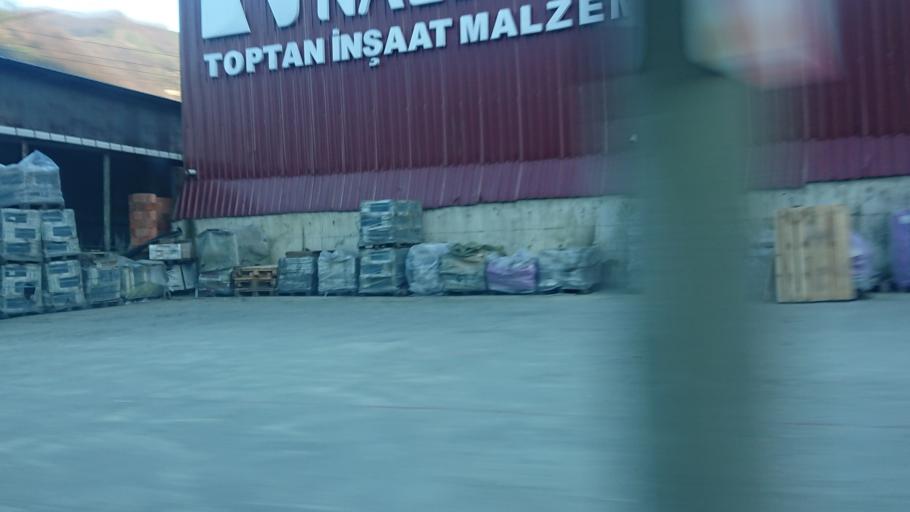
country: TR
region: Rize
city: Gundogdu
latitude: 41.0266
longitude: 40.5801
